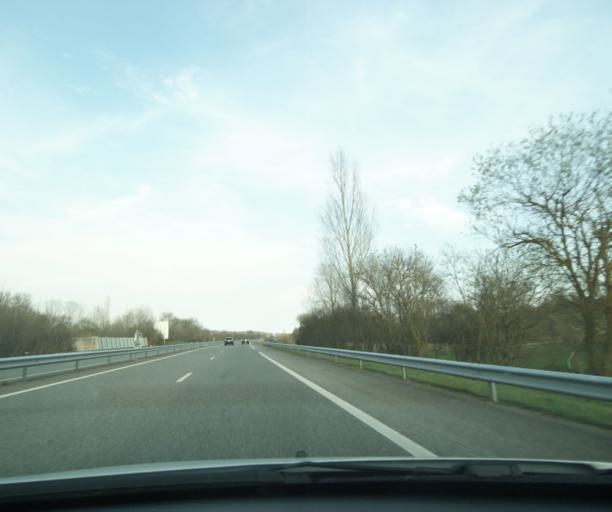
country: FR
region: Midi-Pyrenees
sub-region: Departement de la Haute-Garonne
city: Saint-Gaudens
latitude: 43.1243
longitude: 0.7479
